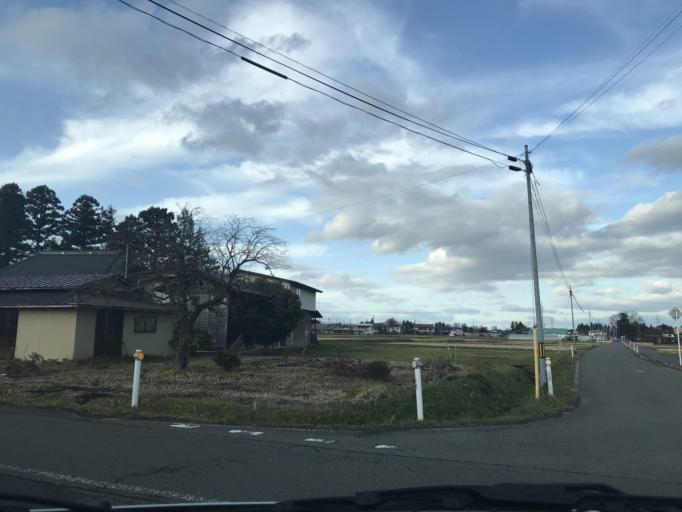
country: JP
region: Iwate
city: Mizusawa
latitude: 39.1871
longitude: 141.1028
